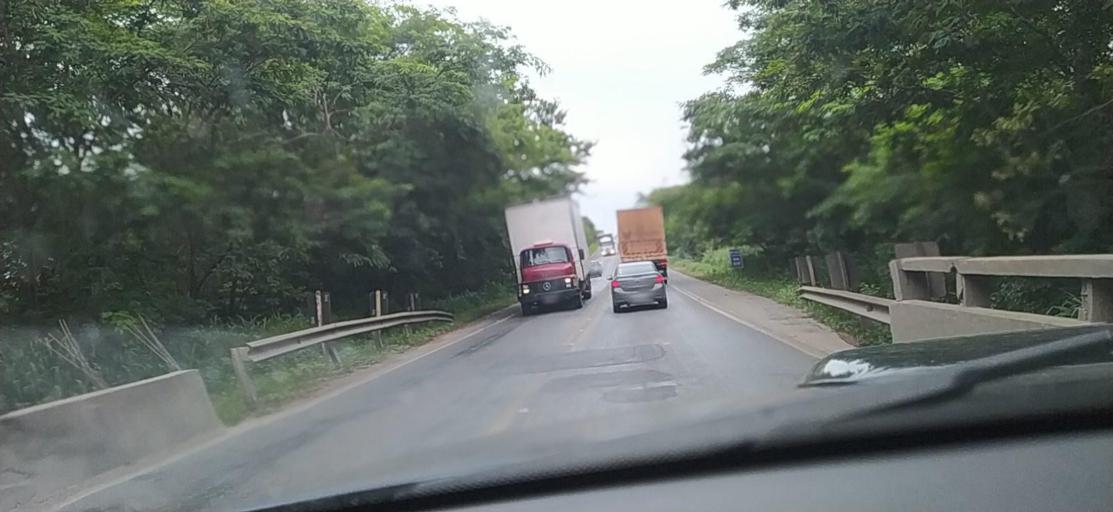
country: BR
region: Minas Gerais
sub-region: Montes Claros
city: Montes Claros
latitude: -16.6600
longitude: -43.7473
